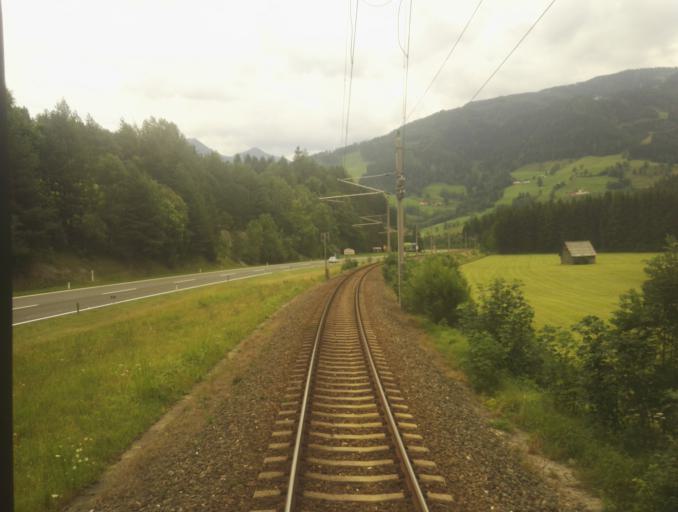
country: AT
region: Salzburg
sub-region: Politischer Bezirk Sankt Johann im Pongau
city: Forstau
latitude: 47.3967
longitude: 13.5907
